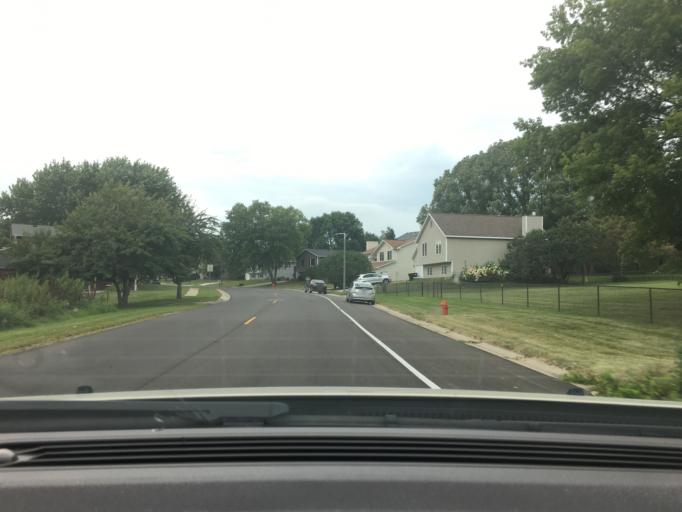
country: US
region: Minnesota
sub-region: Olmsted County
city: Rochester
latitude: 44.0843
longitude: -92.5204
